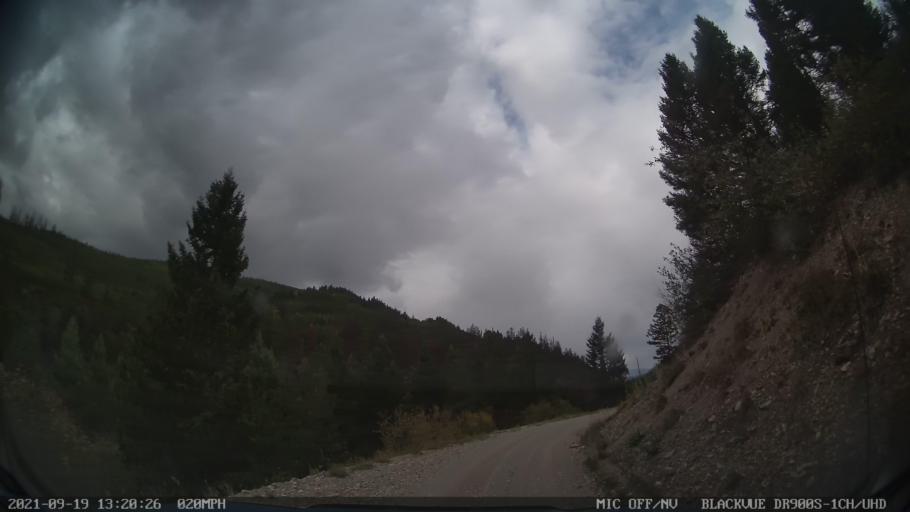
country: US
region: Montana
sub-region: Missoula County
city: Seeley Lake
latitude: 47.1646
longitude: -113.3476
